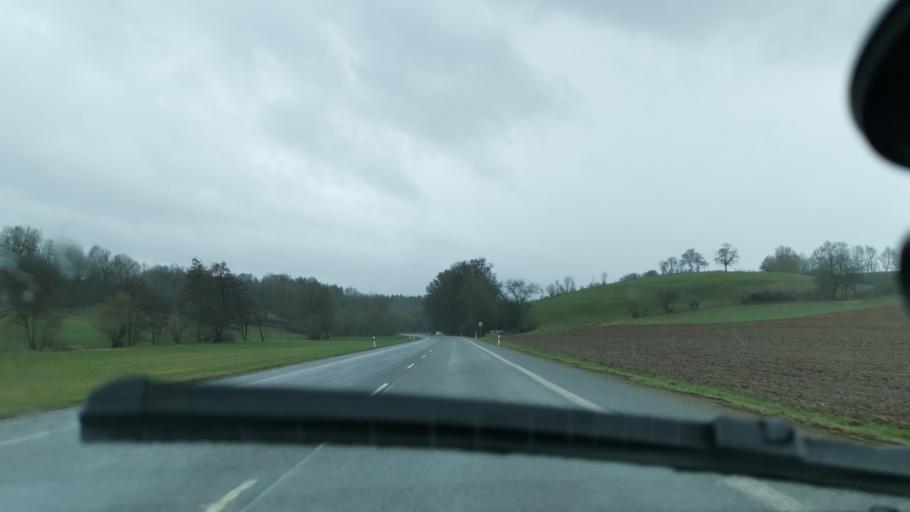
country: DE
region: Hesse
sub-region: Regierungsbezirk Kassel
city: Cornberg
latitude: 51.0524
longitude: 9.8791
